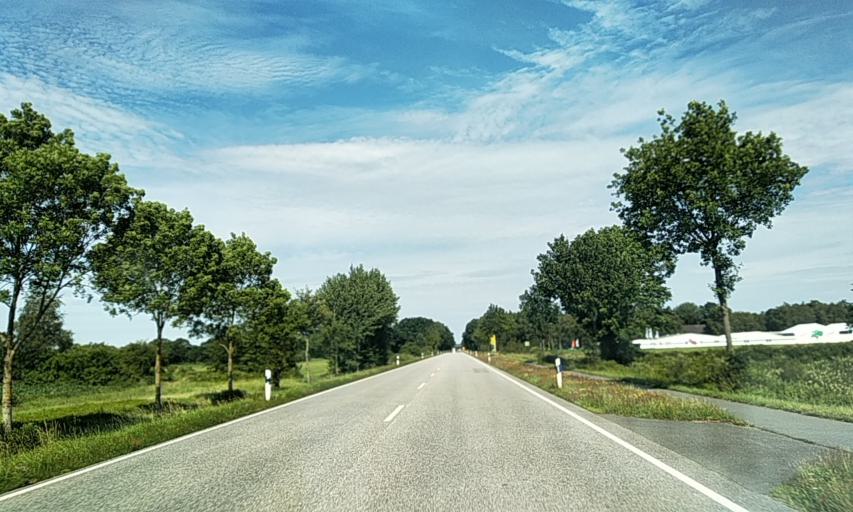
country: DE
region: Schleswig-Holstein
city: Fockbek
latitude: 54.3417
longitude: 9.5985
